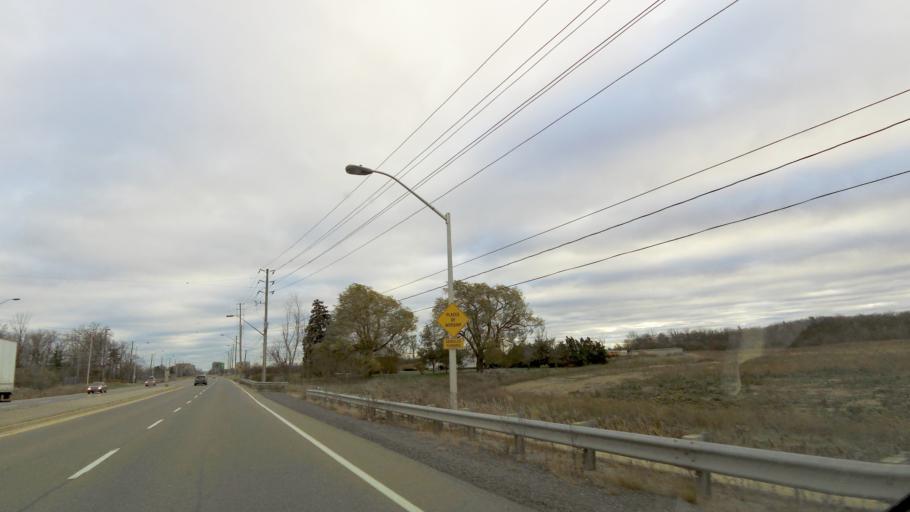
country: CA
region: Ontario
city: Burlington
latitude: 43.4431
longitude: -79.7870
